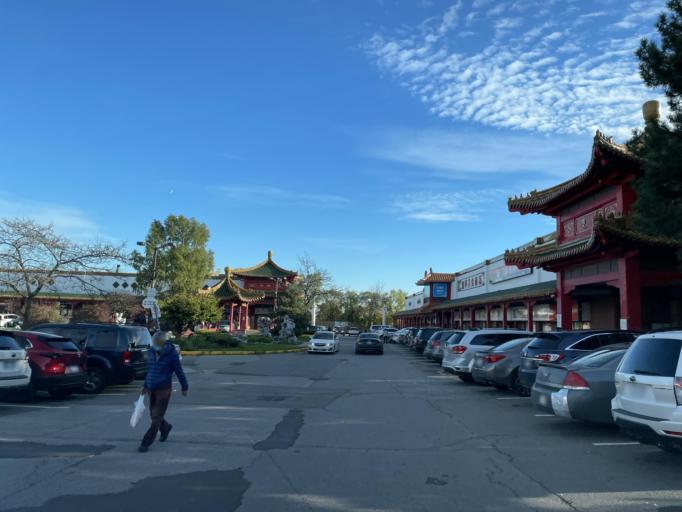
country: CA
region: Ontario
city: Etobicoke
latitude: 43.5979
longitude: -79.5952
